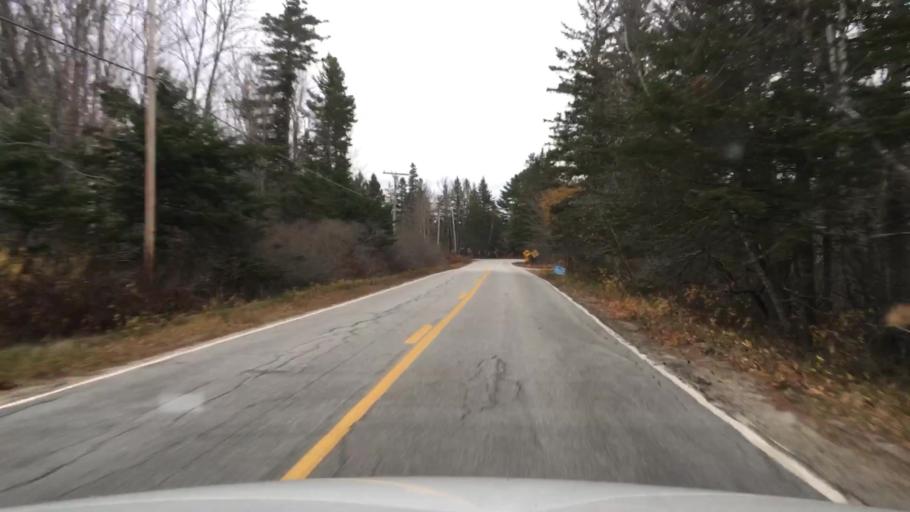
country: US
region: Maine
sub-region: Hancock County
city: Sedgwick
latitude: 44.2755
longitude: -68.5627
